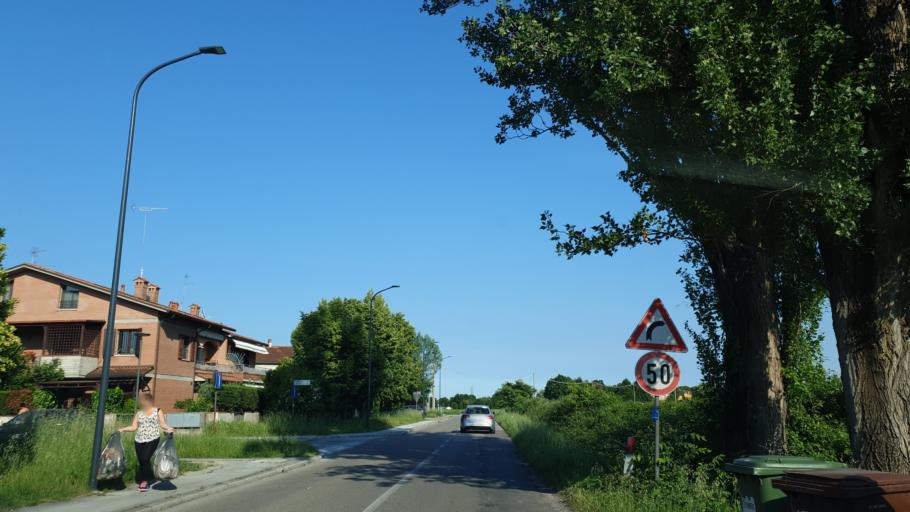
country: IT
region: Emilia-Romagna
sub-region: Provincia di Ravenna
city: Ravenna
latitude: 44.4146
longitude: 12.2228
